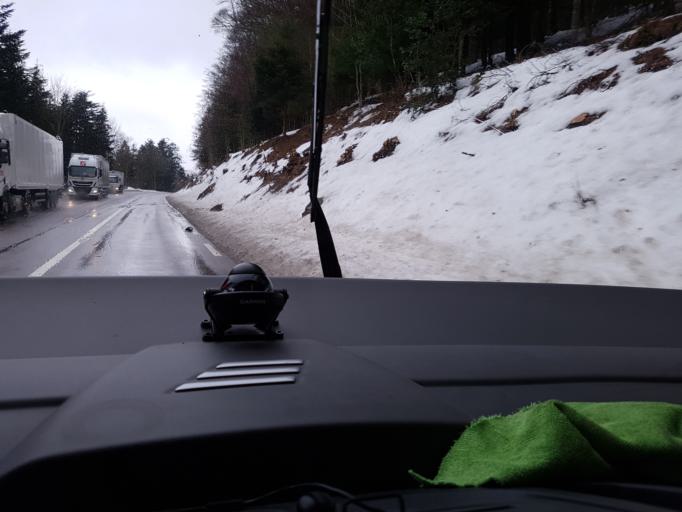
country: FR
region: Lorraine
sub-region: Departement des Vosges
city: Plainfaing
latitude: 48.1670
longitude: 7.0671
